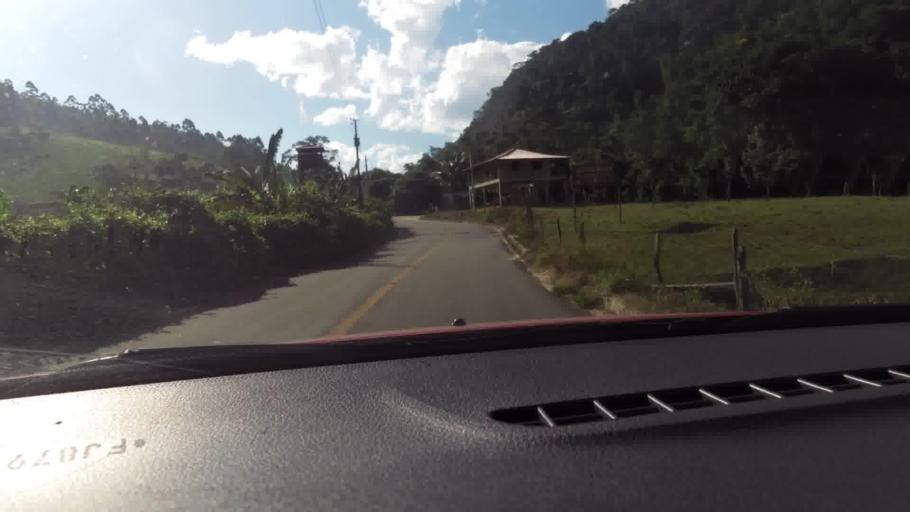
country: BR
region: Espirito Santo
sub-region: Guarapari
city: Guarapari
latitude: -20.5621
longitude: -40.5514
